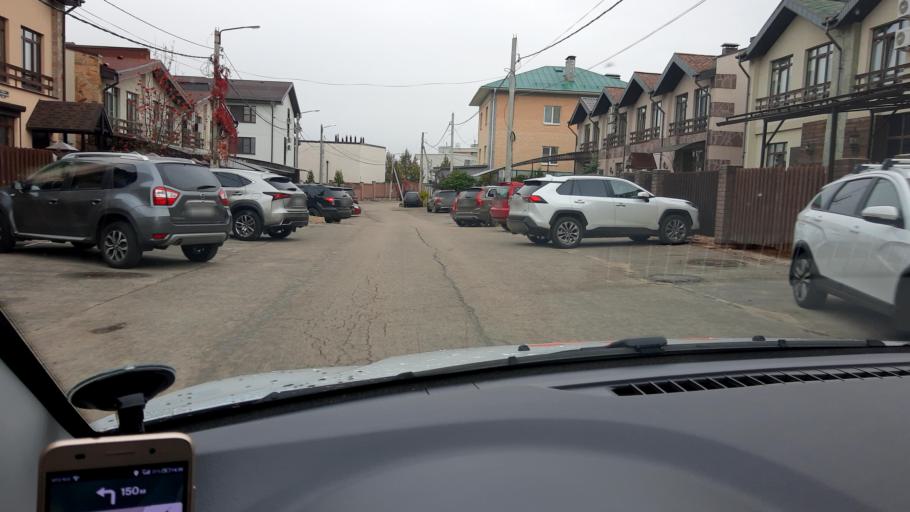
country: RU
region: Nizjnij Novgorod
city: Afonino
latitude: 56.2827
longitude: 44.0740
